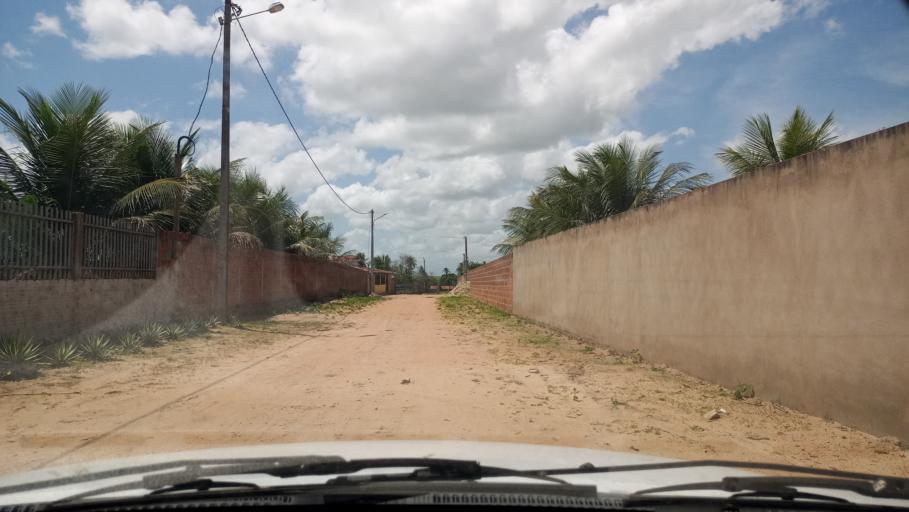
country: BR
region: Rio Grande do Norte
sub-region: Brejinho
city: Brejinho
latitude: -6.2648
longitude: -35.3710
